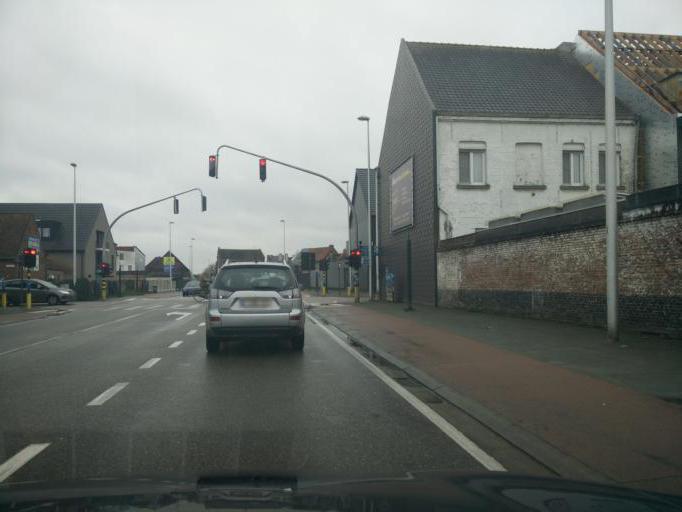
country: BE
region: Flanders
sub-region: Provincie Oost-Vlaanderen
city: Lochristi
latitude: 51.0805
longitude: 3.8806
